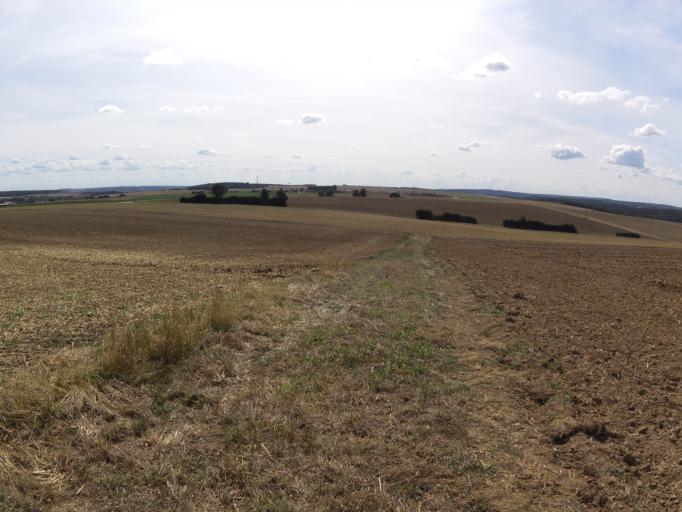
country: DE
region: Bavaria
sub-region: Regierungsbezirk Unterfranken
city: Rimpar
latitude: 49.8617
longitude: 9.9347
